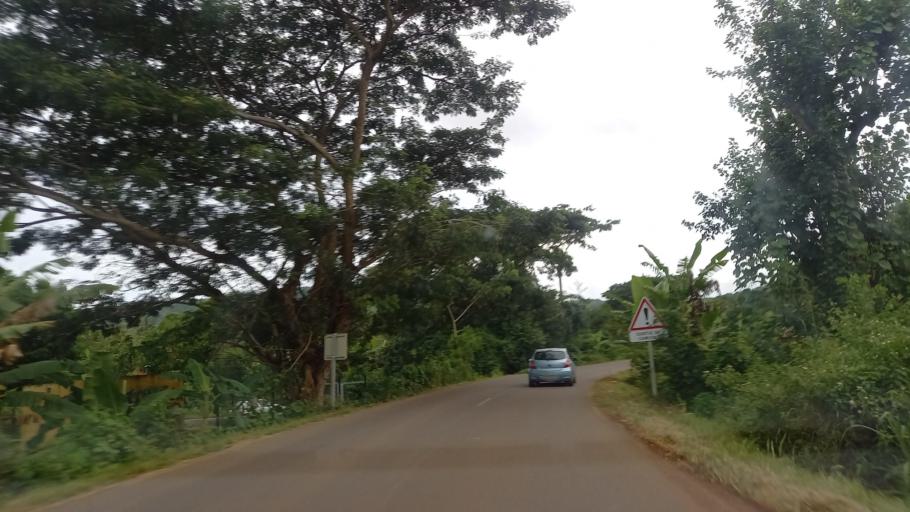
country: YT
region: Chirongui
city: Chirongui
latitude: -12.9067
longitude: 45.1573
